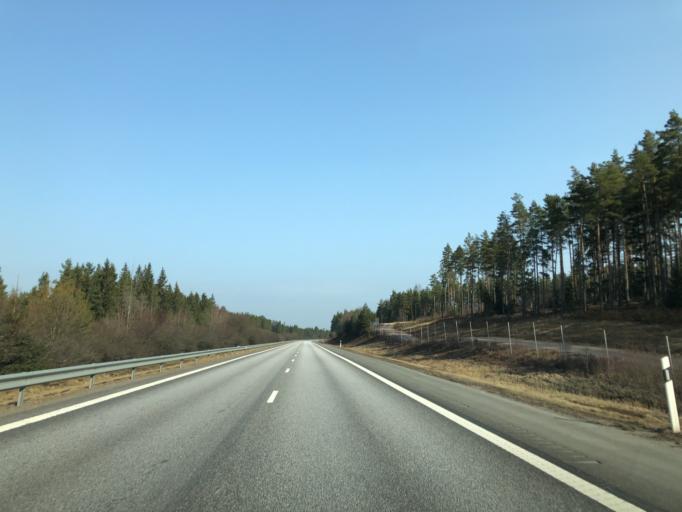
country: SE
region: Joenkoeping
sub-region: Varnamo Kommun
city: Varnamo
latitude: 57.2247
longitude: 14.0803
